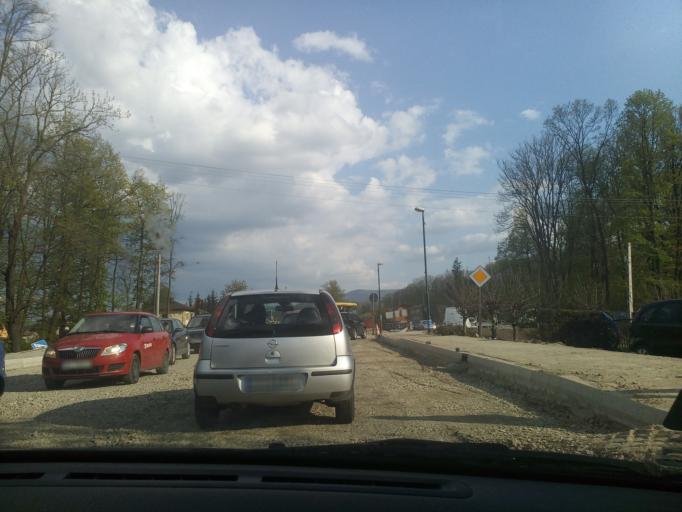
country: PL
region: Lesser Poland Voivodeship
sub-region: Powiat nowosadecki
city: Nawojowa
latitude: 49.5661
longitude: 20.7401
